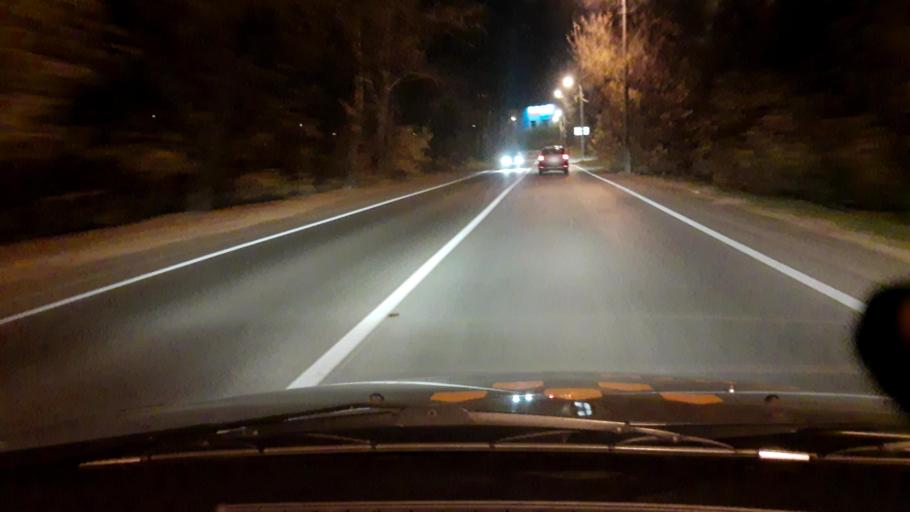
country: RU
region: Bashkortostan
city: Ufa
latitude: 54.8577
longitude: 56.0750
